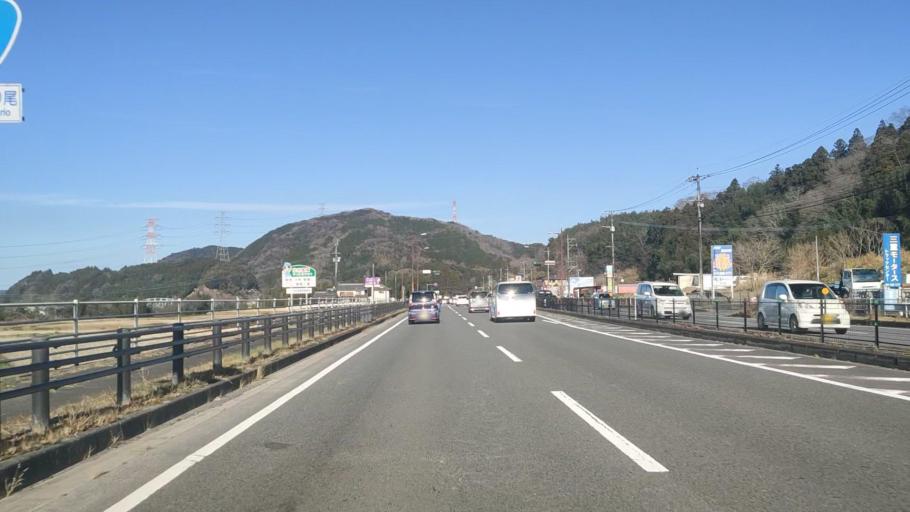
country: JP
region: Oita
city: Oita
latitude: 33.1040
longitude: 131.6531
